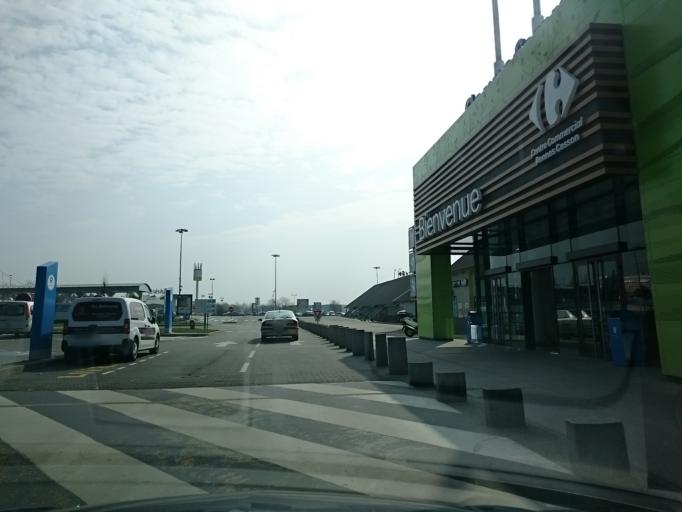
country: FR
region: Brittany
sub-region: Departement d'Ille-et-Vilaine
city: Cesson-Sevigne
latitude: 48.1129
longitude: -1.5908
